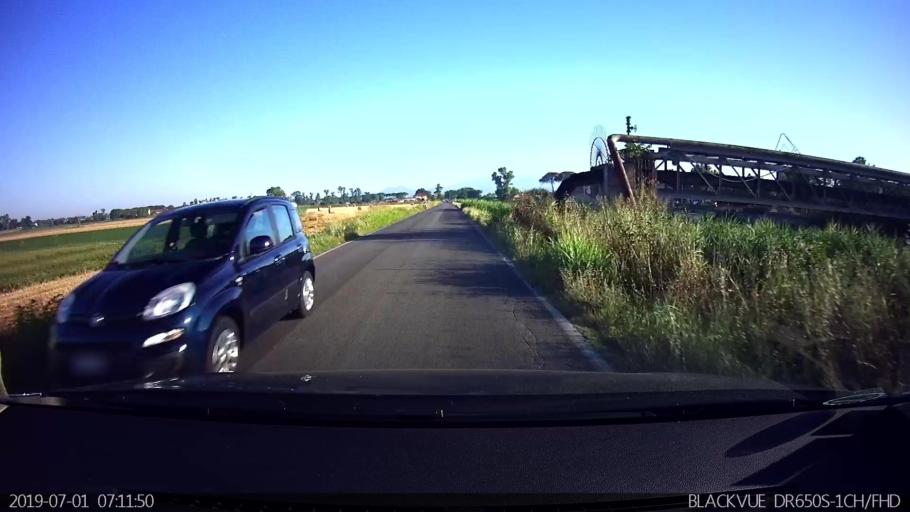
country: IT
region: Latium
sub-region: Provincia di Latina
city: Borgo Hermada
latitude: 41.3244
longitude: 13.1761
